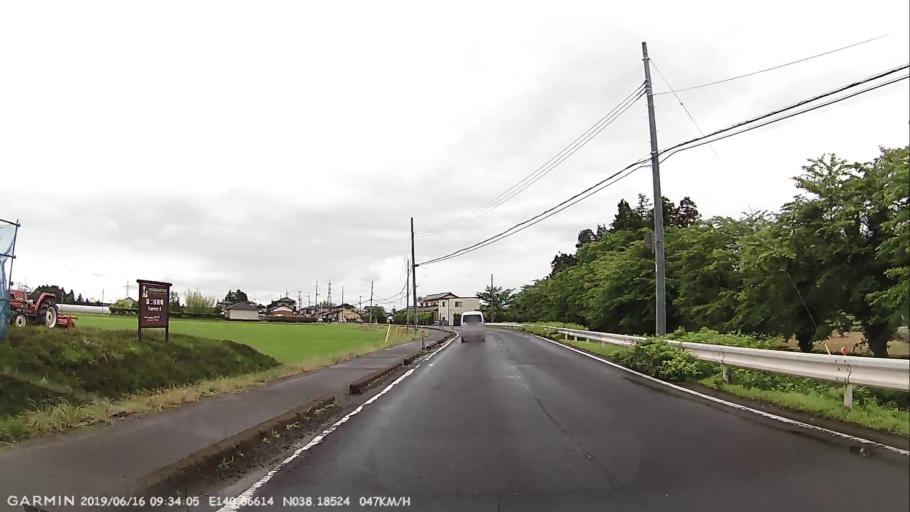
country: JP
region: Miyagi
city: Sendai
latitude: 38.1852
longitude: 140.8661
